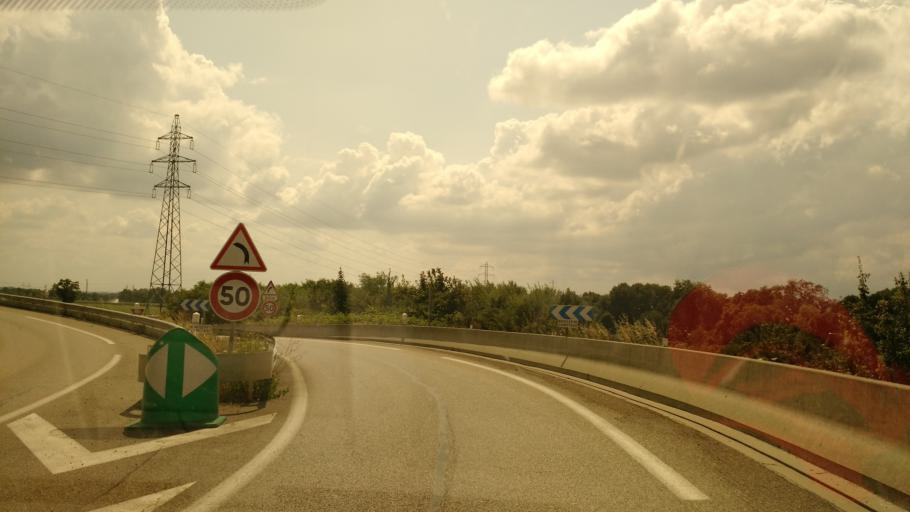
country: FR
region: Rhone-Alpes
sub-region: Departement de l'Ain
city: La Boisse
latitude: 45.8400
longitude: 5.0450
